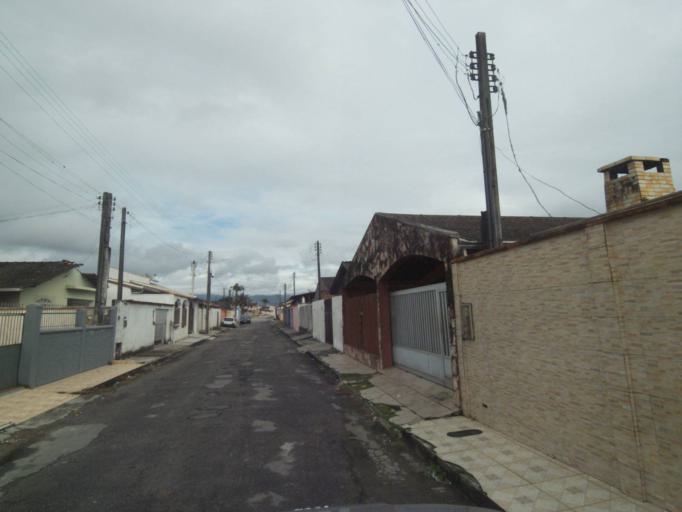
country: BR
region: Parana
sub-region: Paranagua
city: Paranagua
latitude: -25.5659
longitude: -48.5621
